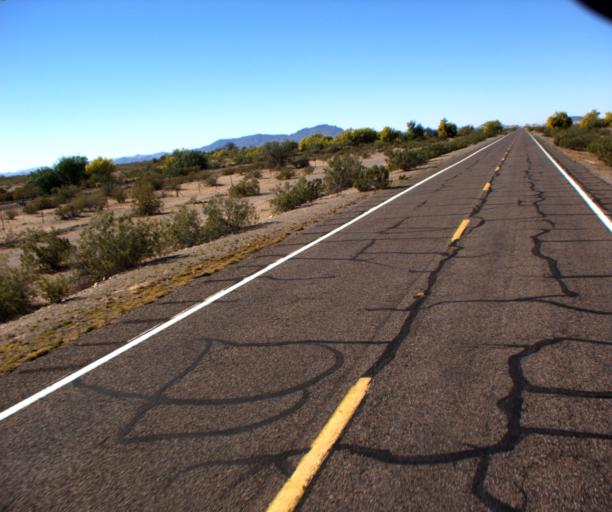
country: US
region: Arizona
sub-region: Maricopa County
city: Gila Bend
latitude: 32.8825
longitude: -112.7532
